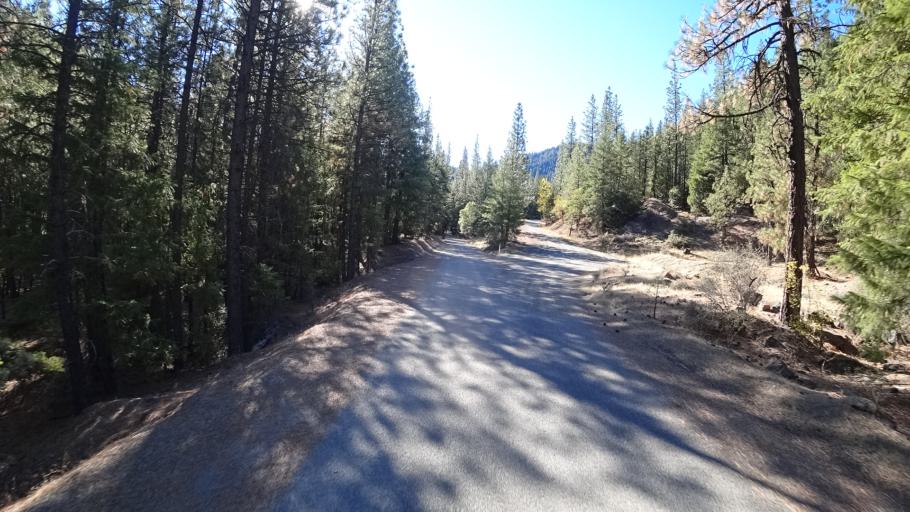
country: US
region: California
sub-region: Trinity County
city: Weaverville
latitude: 41.1088
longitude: -123.0881
